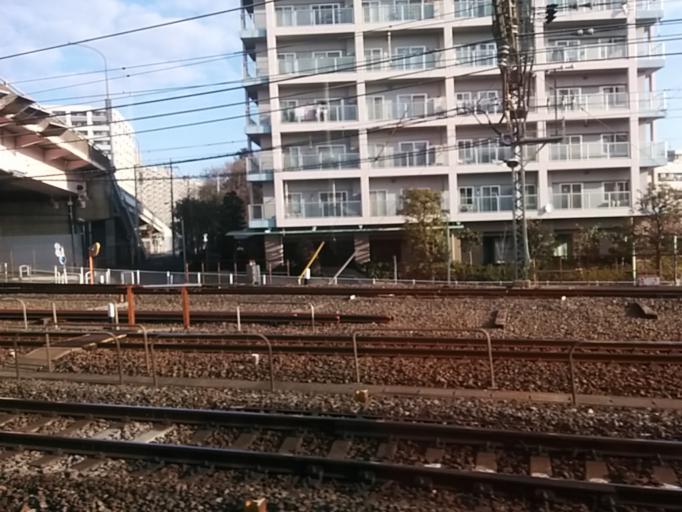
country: JP
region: Saitama
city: Shiki
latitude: 35.8211
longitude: 139.5769
